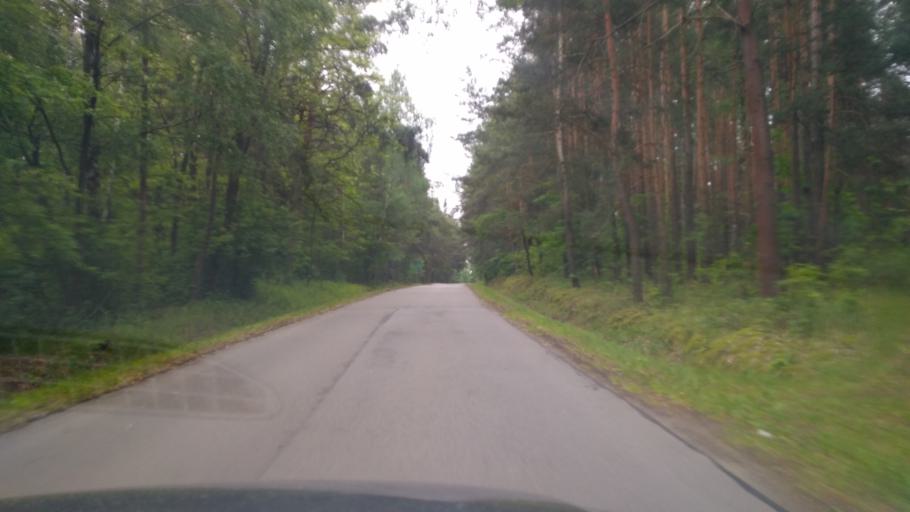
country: PL
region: Subcarpathian Voivodeship
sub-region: Powiat kolbuszowski
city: Niwiska
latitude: 50.2166
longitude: 21.6431
